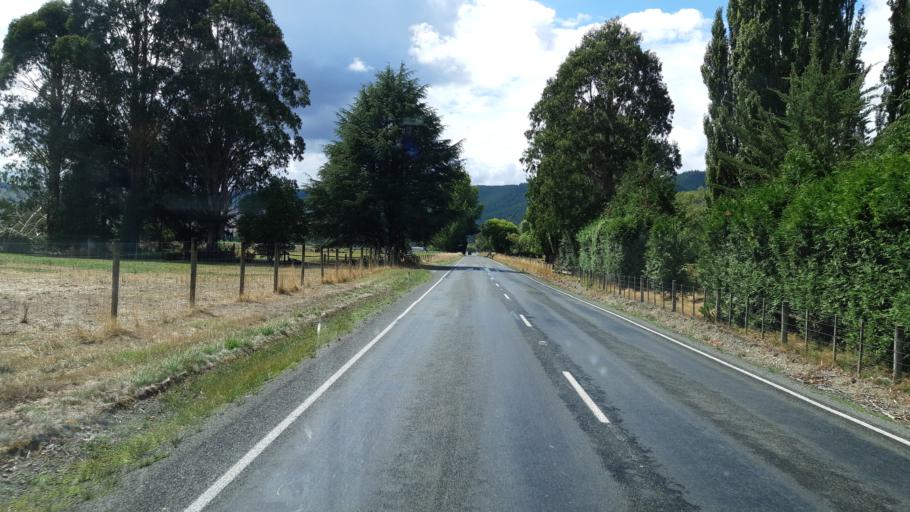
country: NZ
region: Tasman
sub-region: Tasman District
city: Wakefield
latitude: -41.4523
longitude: 172.8214
